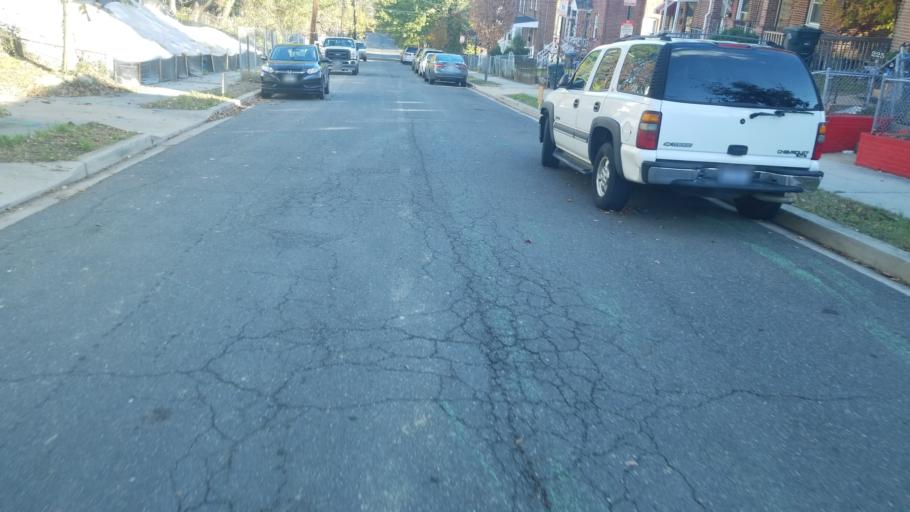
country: US
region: Maryland
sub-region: Prince George's County
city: Capitol Heights
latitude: 38.8915
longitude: -76.9189
